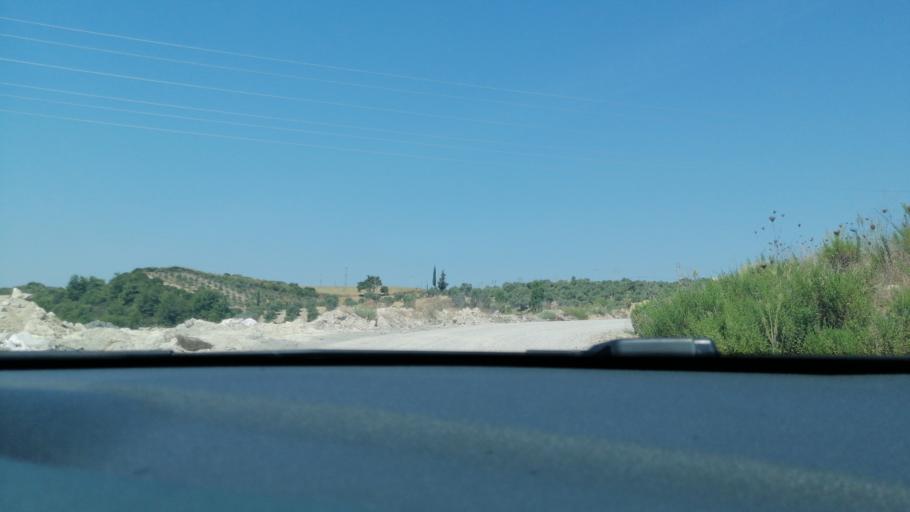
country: TR
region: Aydin
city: Davutlar
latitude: 37.7838
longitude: 27.3158
